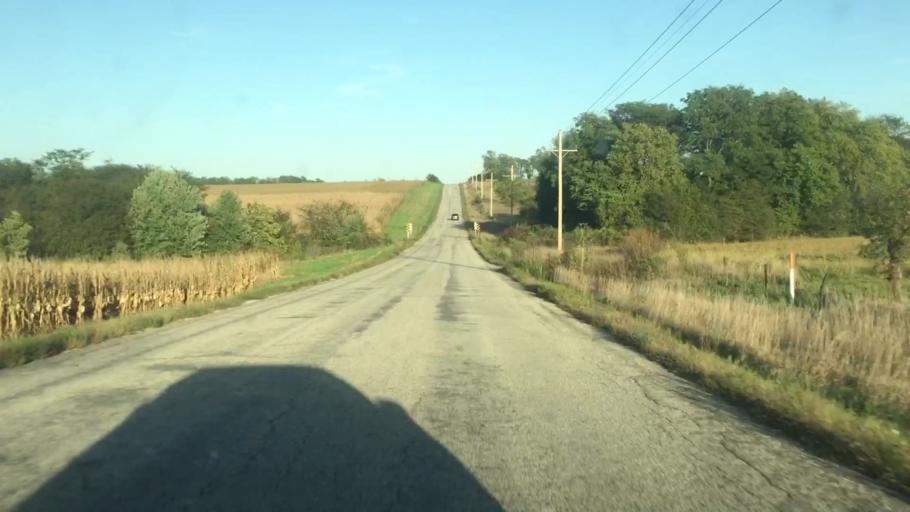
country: US
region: Kansas
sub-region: Brown County
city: Horton
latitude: 39.5656
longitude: -95.3352
